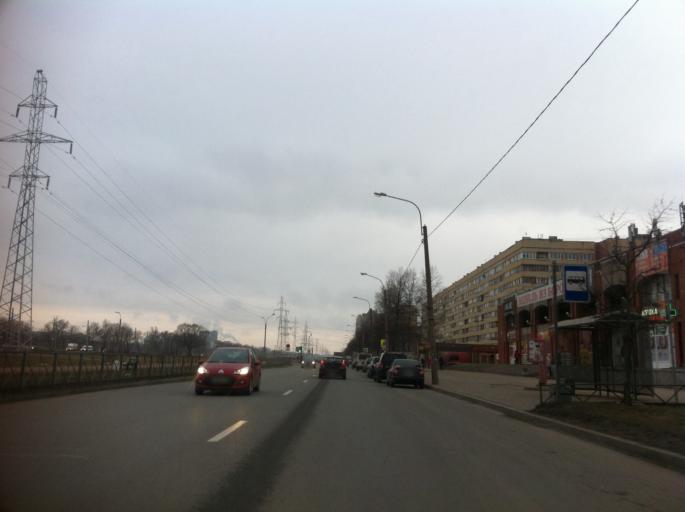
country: RU
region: St.-Petersburg
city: Uritsk
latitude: 59.8466
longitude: 30.2069
